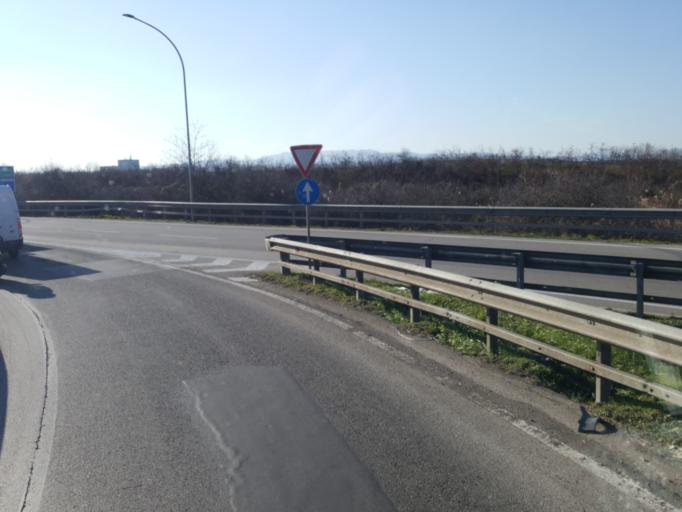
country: IT
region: Tuscany
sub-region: Province of Florence
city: Sesto Fiorentino
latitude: 43.8163
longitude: 11.1865
